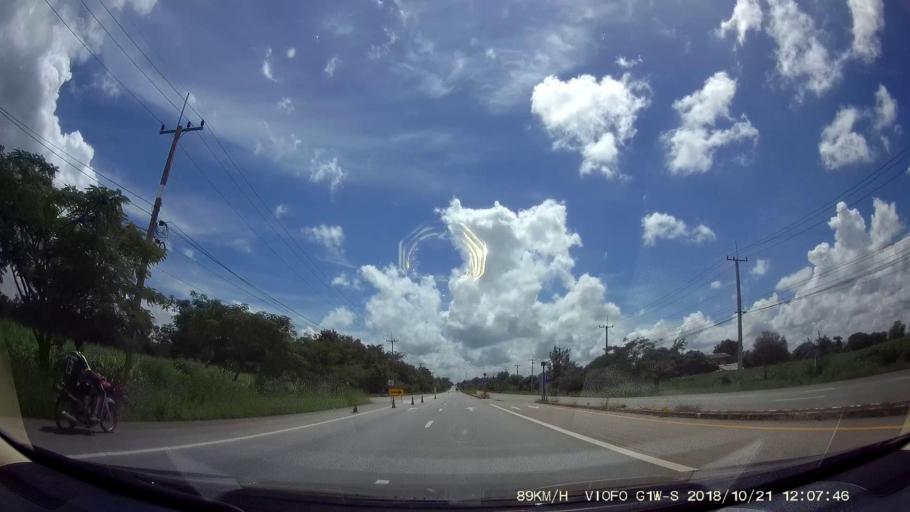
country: TH
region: Chaiyaphum
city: Chatturat
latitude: 15.4438
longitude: 101.8290
